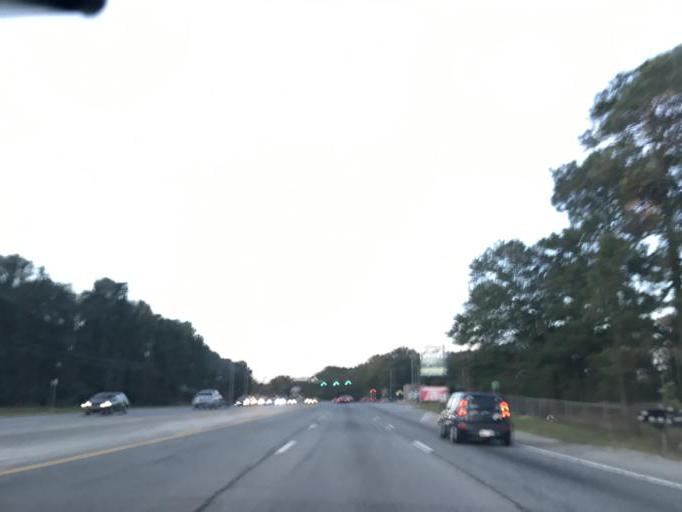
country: US
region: Georgia
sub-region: Bibb County
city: Macon
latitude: 32.7421
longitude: -83.6552
